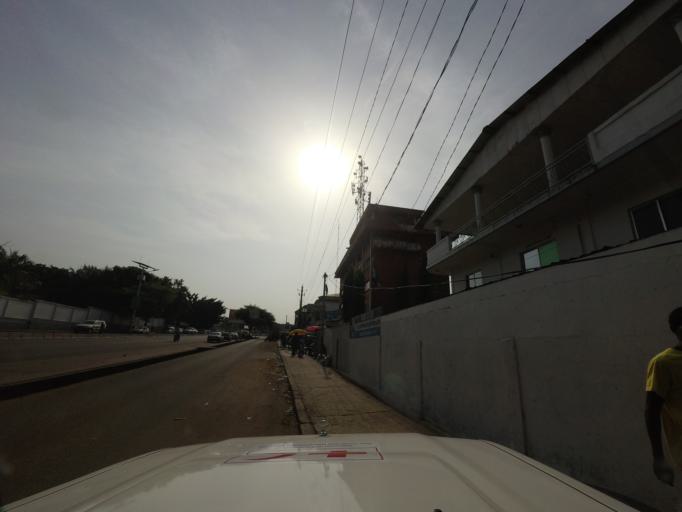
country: GN
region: Conakry
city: Conakry
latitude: 9.5579
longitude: -13.6676
